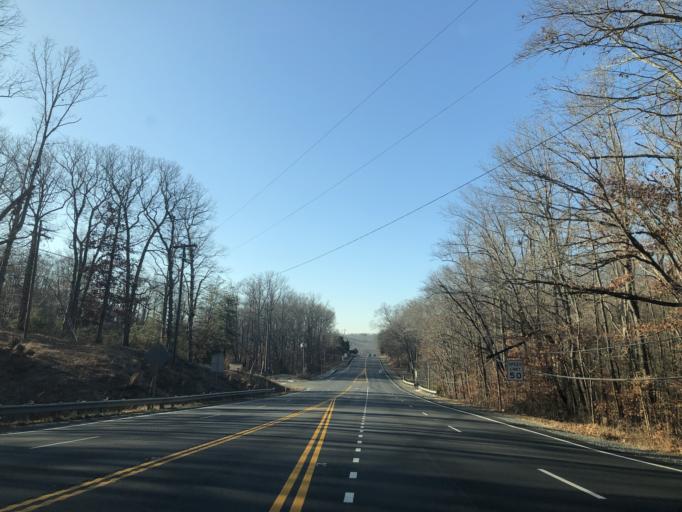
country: US
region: Virginia
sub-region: Stafford County
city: Stafford
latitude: 38.4106
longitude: -77.4136
